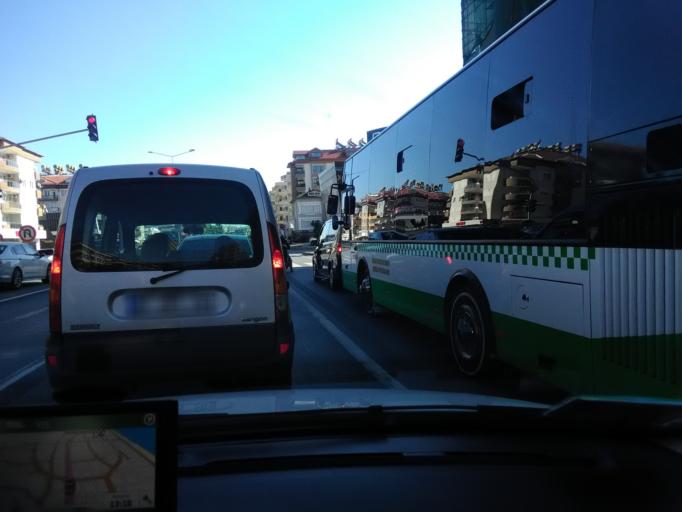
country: TR
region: Antalya
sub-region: Alanya
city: Alanya
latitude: 36.5399
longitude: 32.0373
